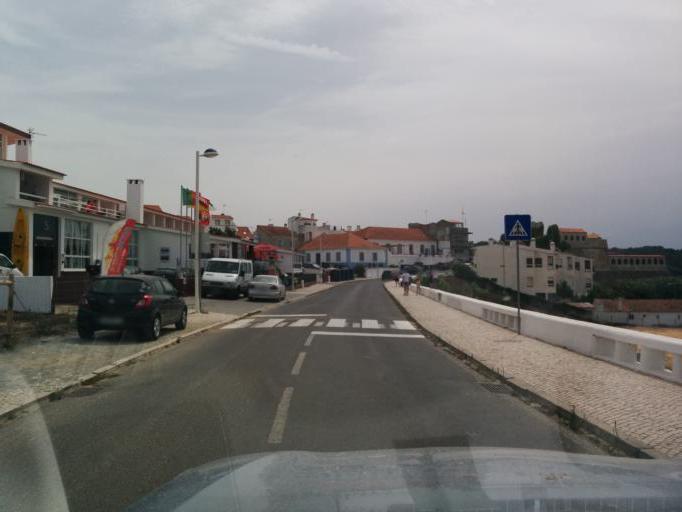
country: PT
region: Beja
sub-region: Odemira
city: Vila Nova de Milfontes
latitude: 37.7236
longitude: -8.7847
